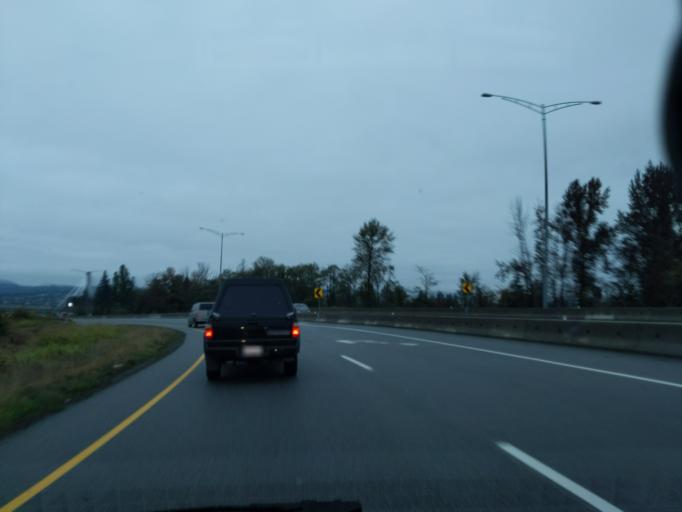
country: CA
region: British Columbia
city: Coquitlam
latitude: 49.2024
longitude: -122.7978
